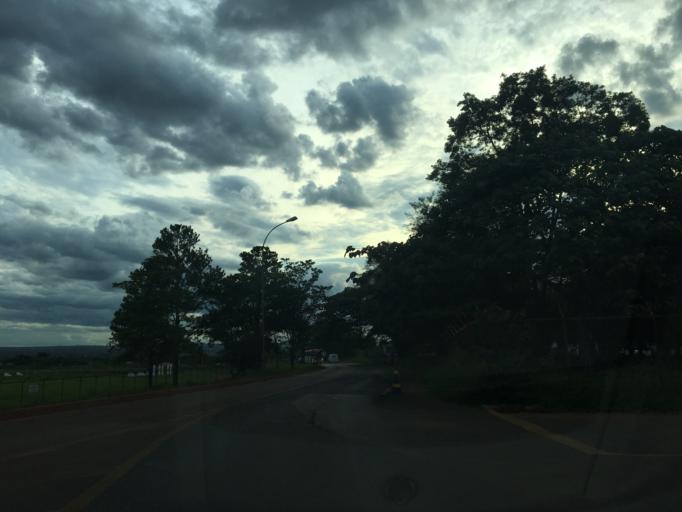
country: BR
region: Federal District
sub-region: Brasilia
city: Brasilia
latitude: -15.8313
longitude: -47.9308
